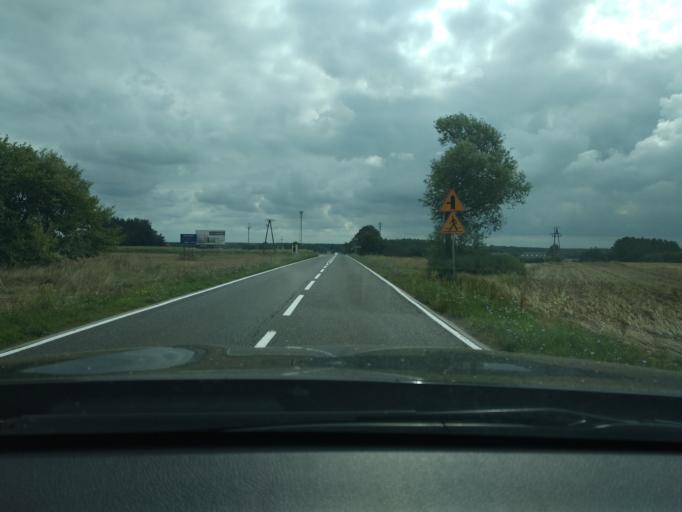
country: PL
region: Masovian Voivodeship
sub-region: Powiat pultuski
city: Obryte
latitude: 52.6539
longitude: 21.2339
